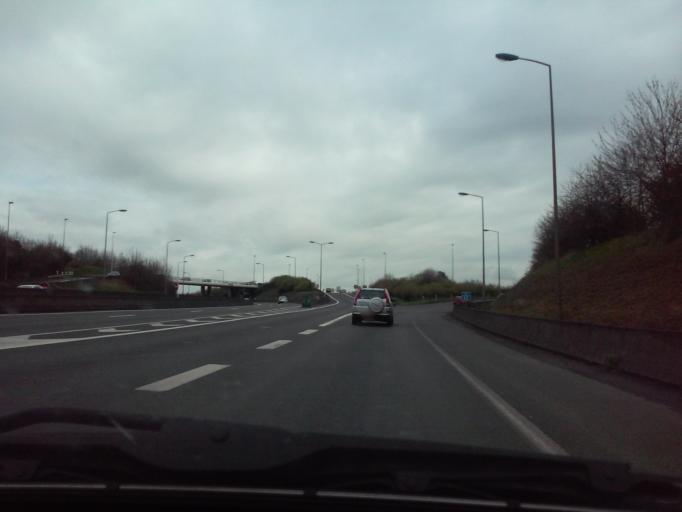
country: FR
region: Lower Normandy
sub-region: Departement du Calvados
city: Mondeville
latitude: 49.1667
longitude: -0.3032
